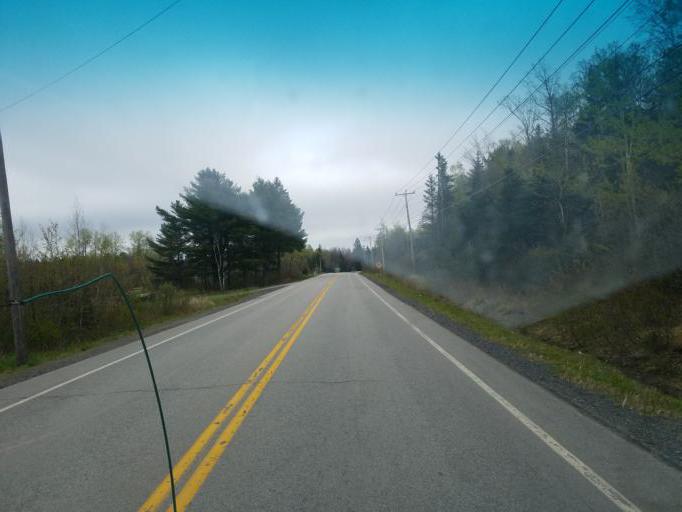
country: US
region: Maine
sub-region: Washington County
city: Eastport
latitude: 44.8002
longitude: -67.1406
